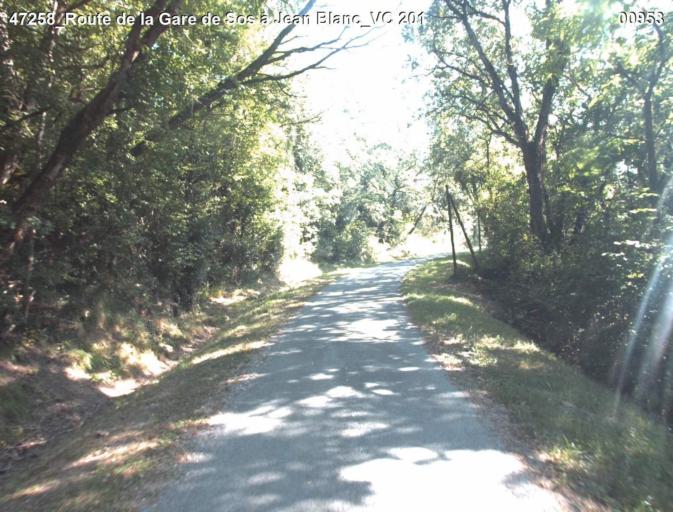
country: FR
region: Midi-Pyrenees
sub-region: Departement du Gers
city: Montreal
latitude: 44.0353
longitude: 0.1492
